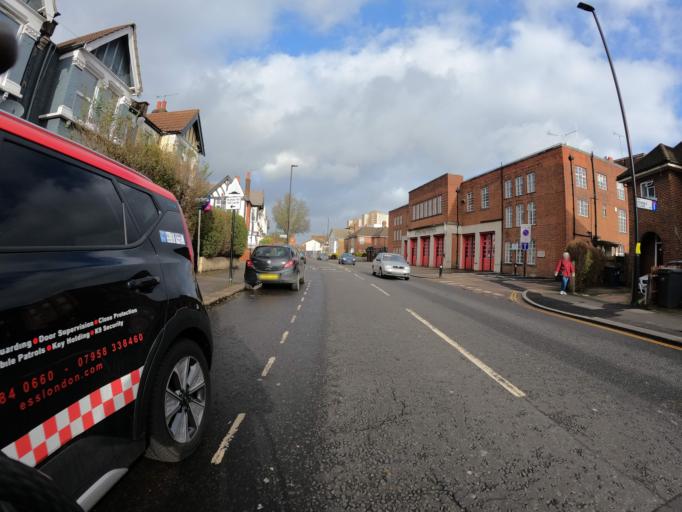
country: GB
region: England
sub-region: Greater London
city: Acton
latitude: 51.5069
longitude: -0.2776
